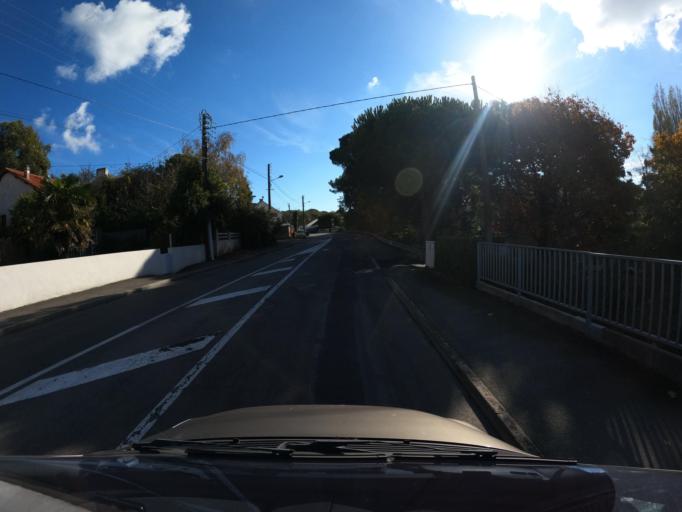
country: FR
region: Pays de la Loire
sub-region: Departement de la Loire-Atlantique
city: La Baule-Escoublac
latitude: 47.2893
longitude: -2.3711
